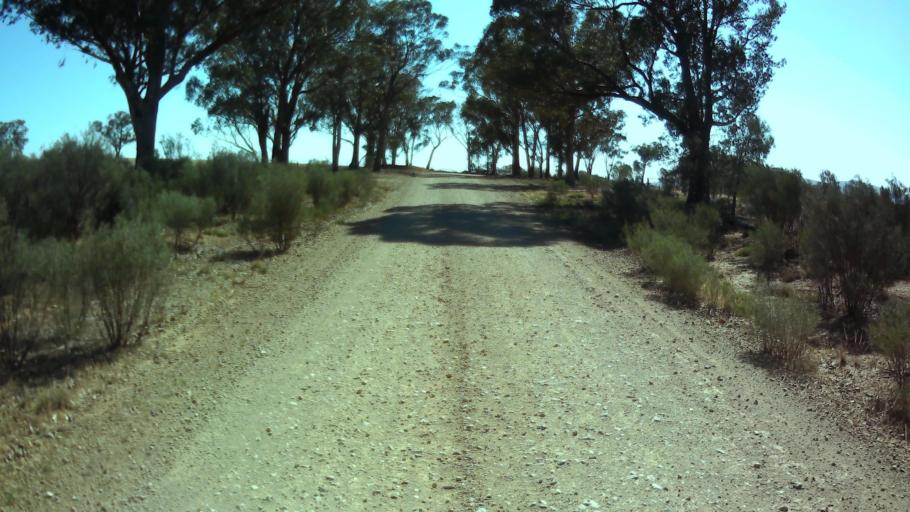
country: AU
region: New South Wales
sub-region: Weddin
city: Grenfell
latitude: -33.9022
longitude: 147.8658
